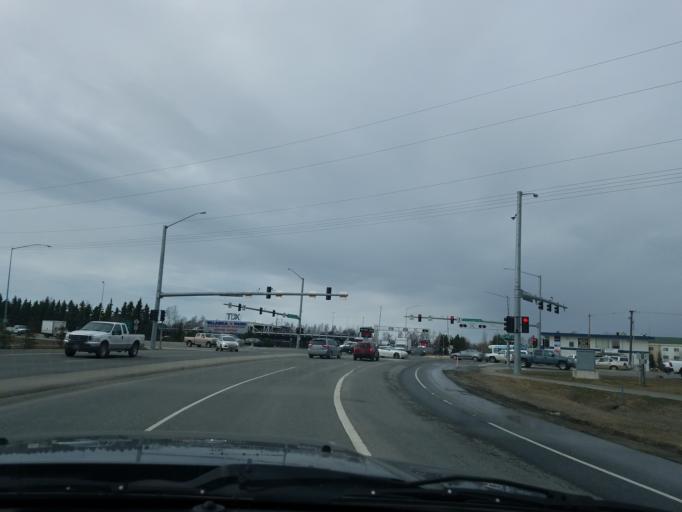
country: US
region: Alaska
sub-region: Anchorage Municipality
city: Anchorage
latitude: 61.1732
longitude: -149.9430
